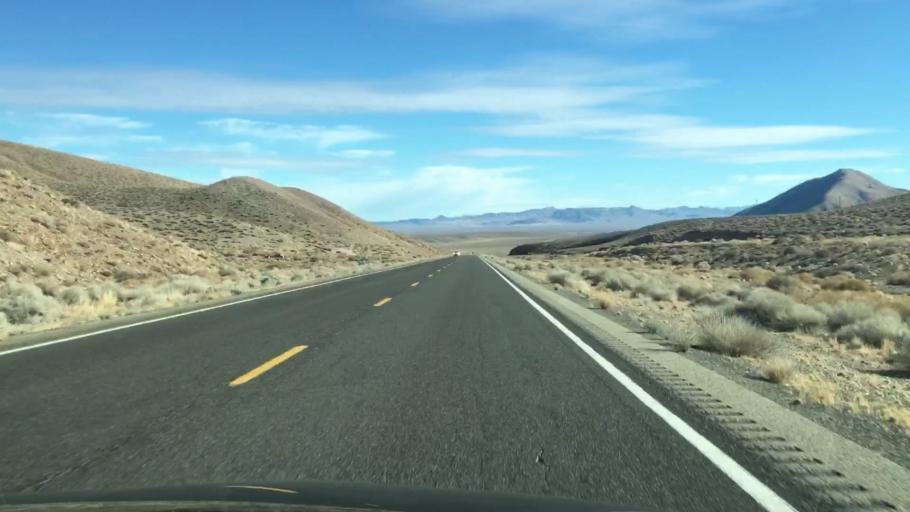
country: US
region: Nevada
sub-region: Lyon County
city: Yerington
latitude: 39.0389
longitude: -118.9352
